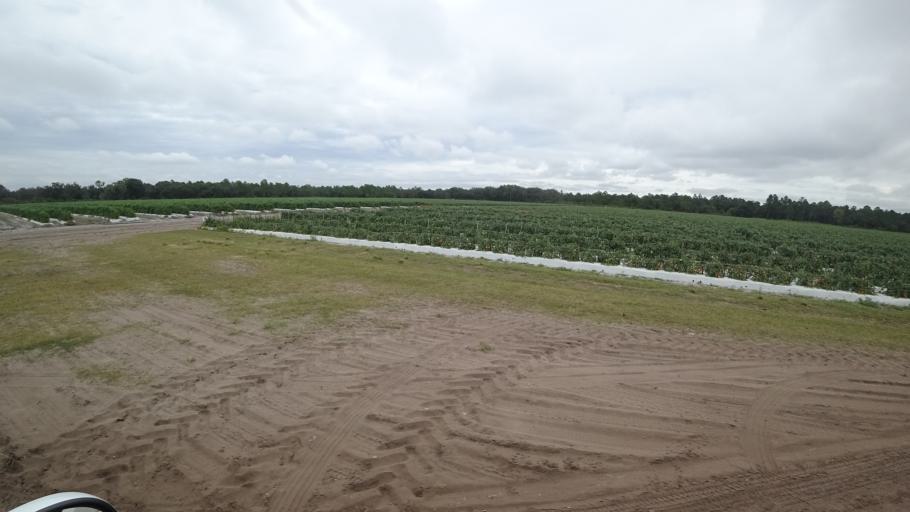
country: US
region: Florida
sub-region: Hillsborough County
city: Wimauma
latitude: 27.5672
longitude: -82.1370
